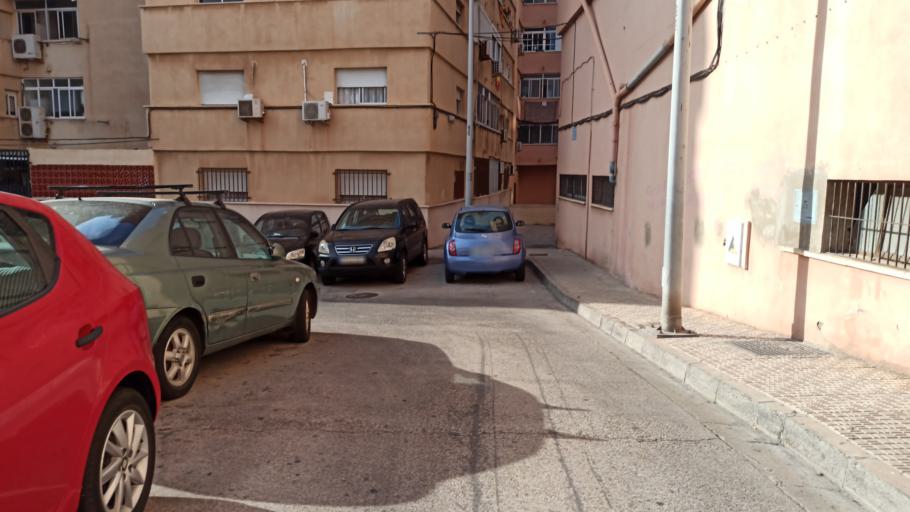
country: ES
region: Melilla
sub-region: Melilla
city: Melilla
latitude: 35.2884
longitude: -2.9538
